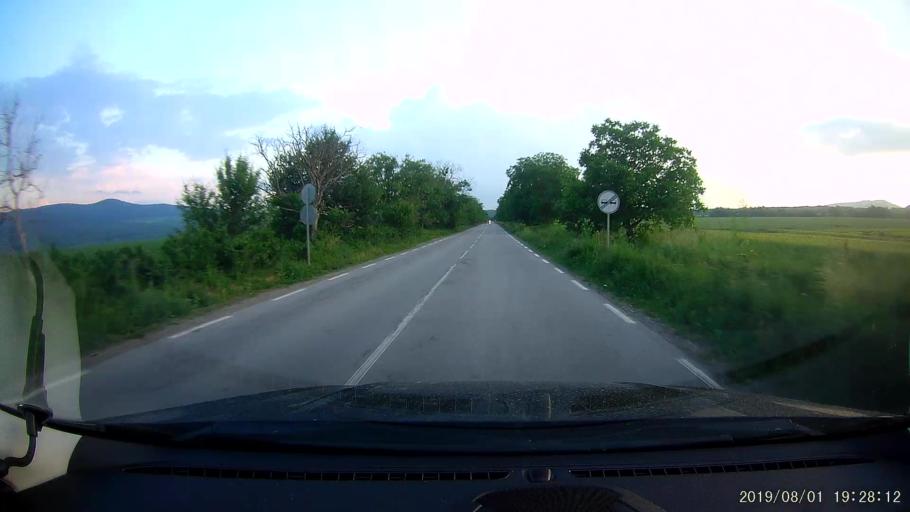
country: BG
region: Burgas
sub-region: Obshtina Sungurlare
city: Sungurlare
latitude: 42.8454
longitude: 26.9221
